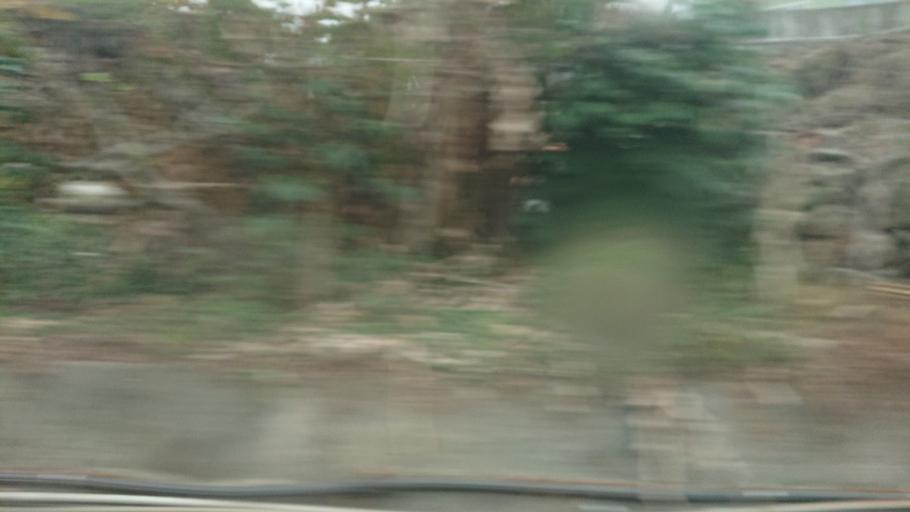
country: TW
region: Taiwan
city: Lugu
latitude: 23.6073
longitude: 120.7088
